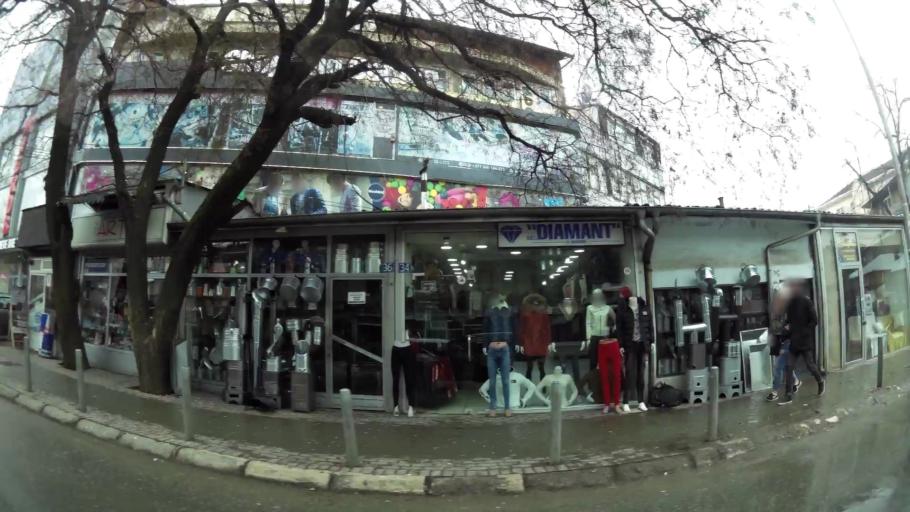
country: XK
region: Pristina
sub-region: Komuna e Prishtines
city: Pristina
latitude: 42.6685
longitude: 21.1640
